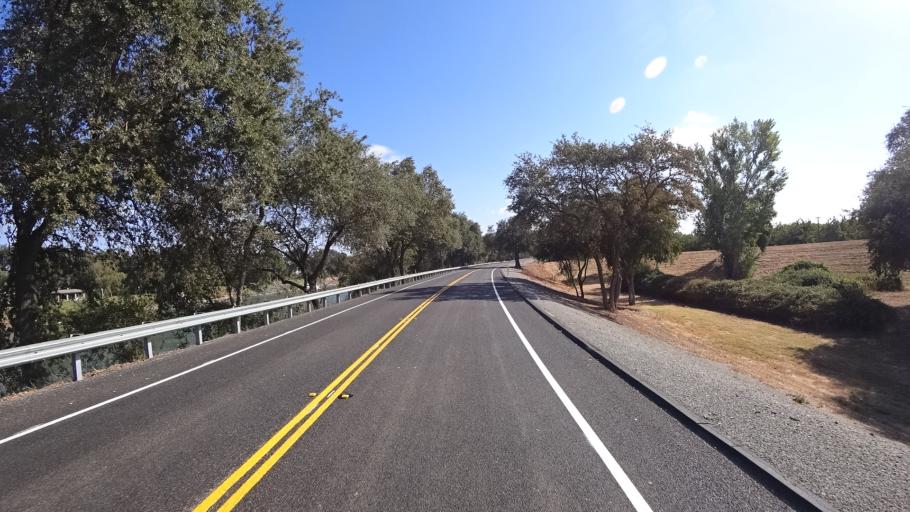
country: US
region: California
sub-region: Yolo County
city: West Sacramento
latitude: 38.6479
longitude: -121.5733
